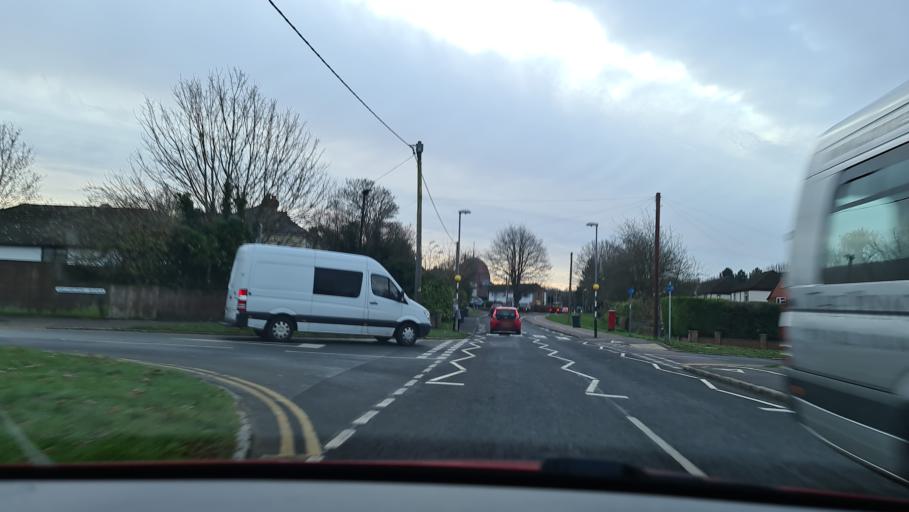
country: GB
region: England
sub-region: Buckinghamshire
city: Princes Risborough
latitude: 51.7277
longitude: -0.8338
